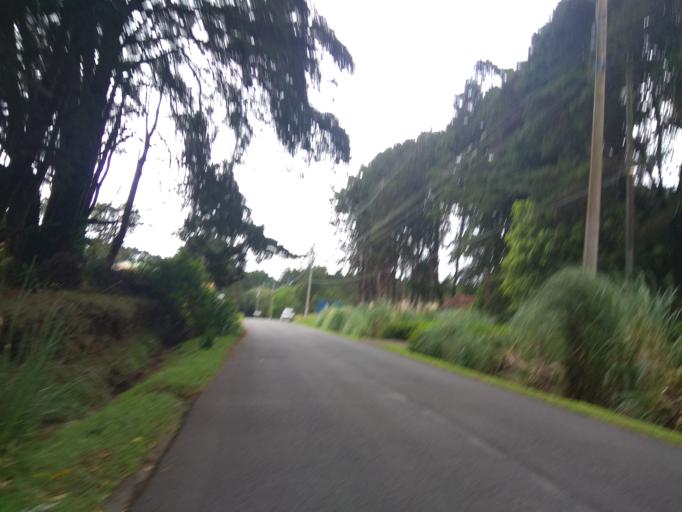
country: CR
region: Heredia
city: San Josecito
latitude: 10.0665
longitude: -84.0848
